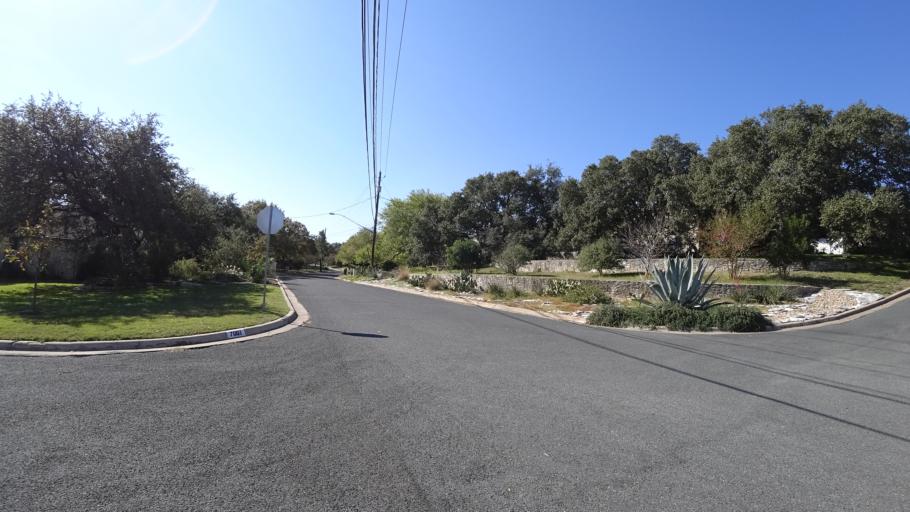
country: US
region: Texas
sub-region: Travis County
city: Barton Creek
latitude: 30.2313
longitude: -97.8693
